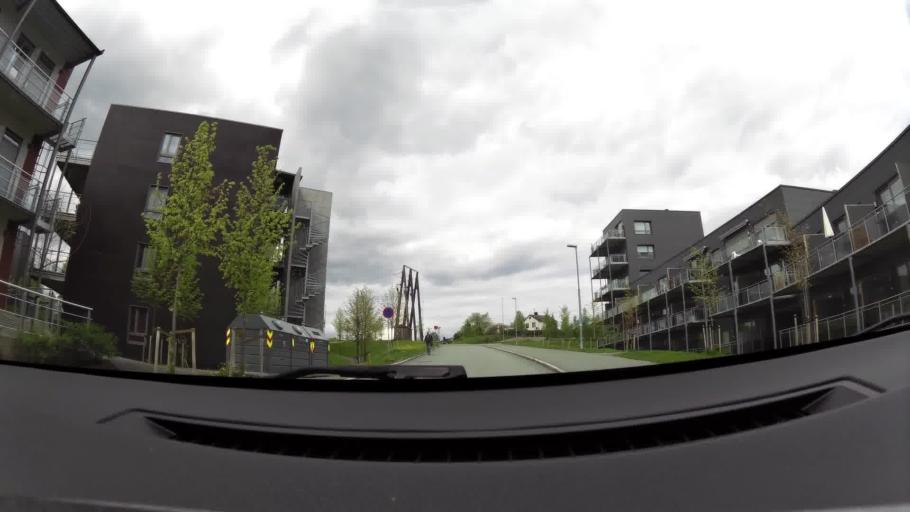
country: NO
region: Sor-Trondelag
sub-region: Trondheim
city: Trondheim
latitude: 63.3902
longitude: 10.4345
